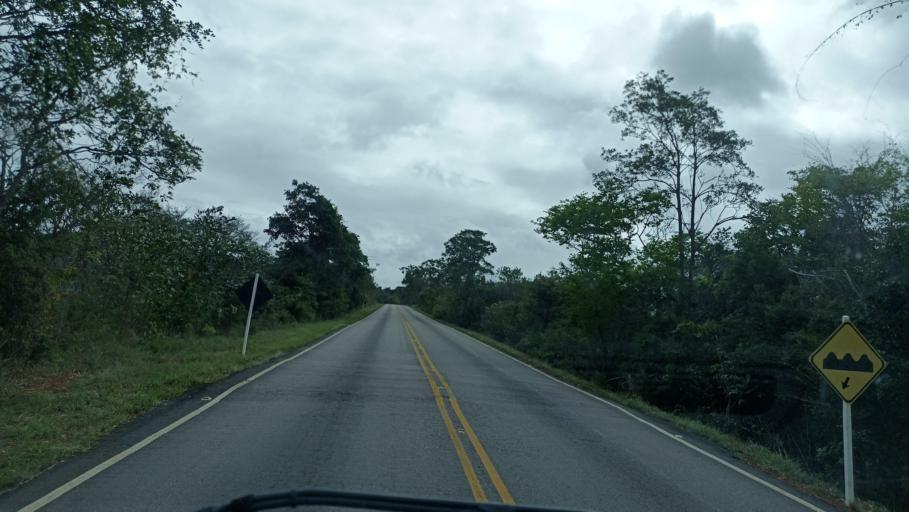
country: BR
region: Bahia
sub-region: Andarai
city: Vera Cruz
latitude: -12.9303
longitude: -41.2451
